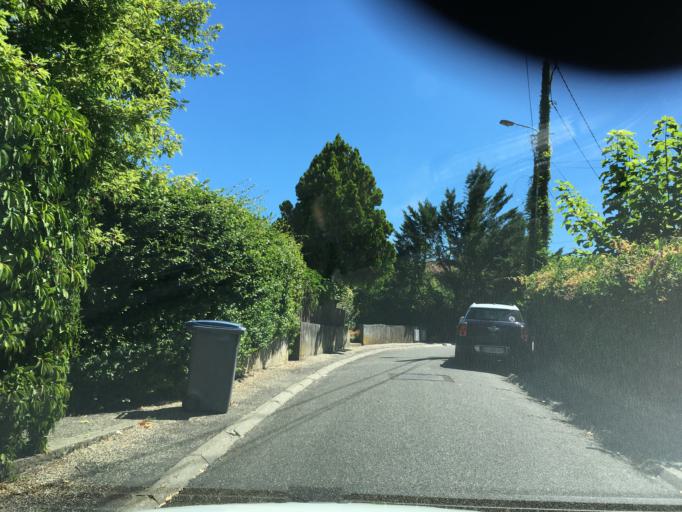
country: FR
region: Midi-Pyrenees
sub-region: Departement du Tarn-et-Garonne
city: Montauban
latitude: 44.0066
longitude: 1.3740
